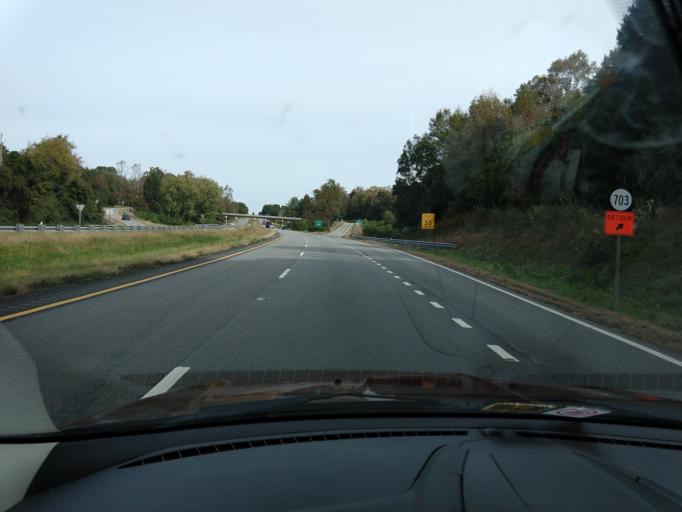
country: US
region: Virginia
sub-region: Pittsylvania County
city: Chatham
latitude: 36.8245
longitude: -79.3811
